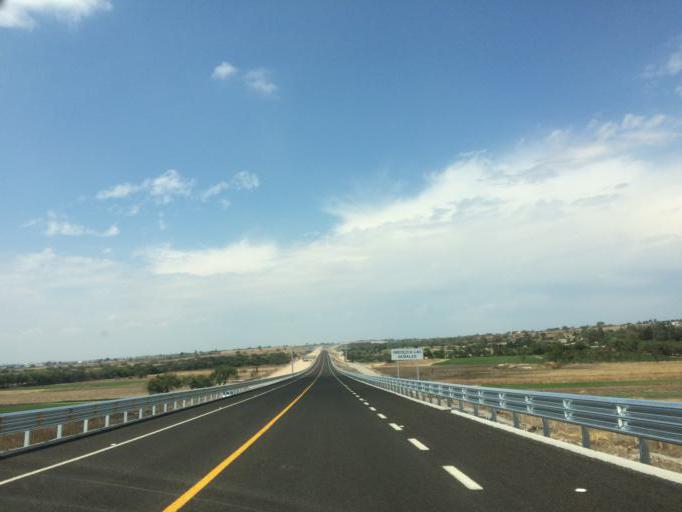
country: MX
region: Guanajuato
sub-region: Silao de la Victoria
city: San Francisco (Banos de Agua Caliente)
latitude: 21.0343
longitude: -101.4845
